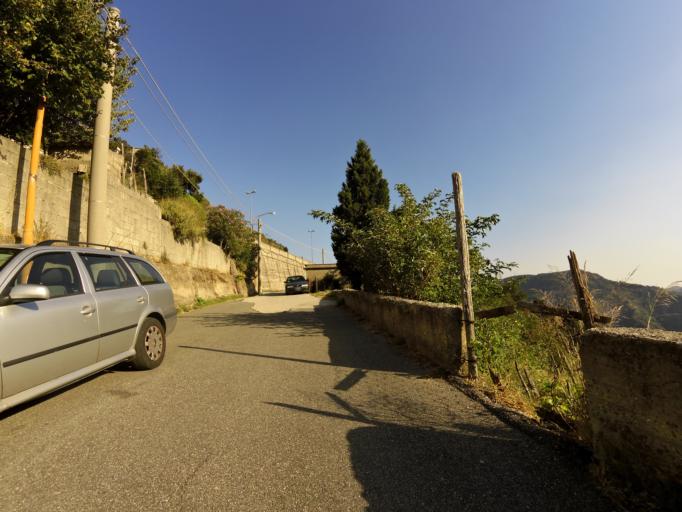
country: IT
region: Calabria
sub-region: Provincia di Reggio Calabria
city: Pazzano
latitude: 38.4498
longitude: 16.4127
